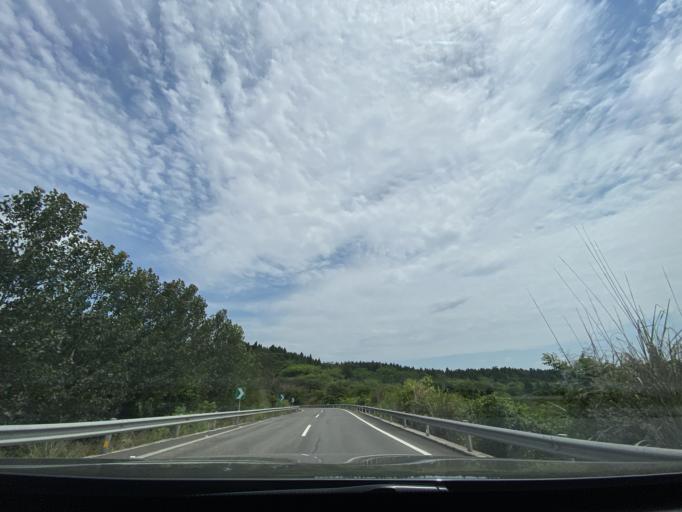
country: CN
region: Sichuan
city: Mianyang
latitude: 31.3504
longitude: 104.7060
